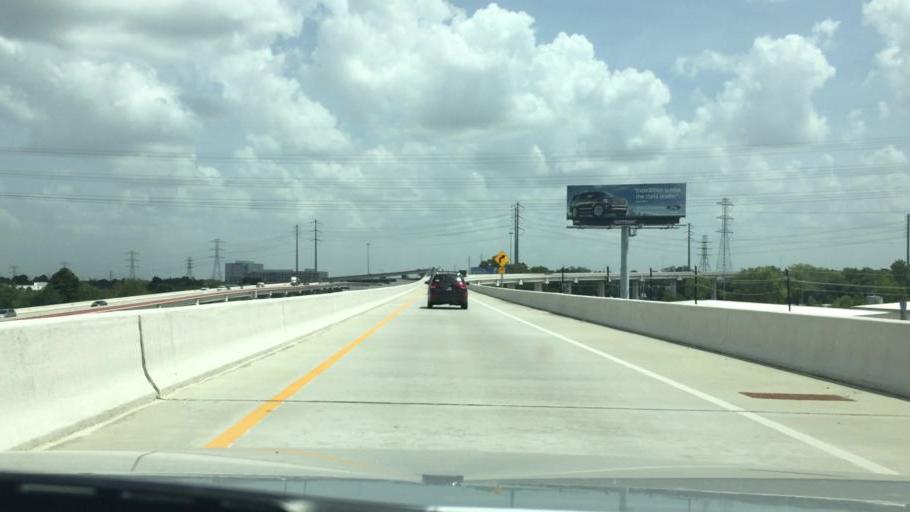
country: US
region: Texas
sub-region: Harris County
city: Hudson
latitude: 29.9421
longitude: -95.5235
